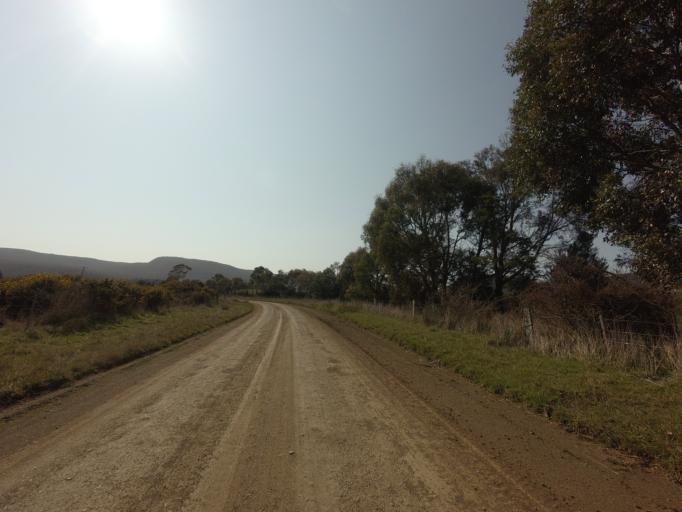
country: AU
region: Tasmania
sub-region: Break O'Day
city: St Helens
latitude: -41.8117
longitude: 147.9422
